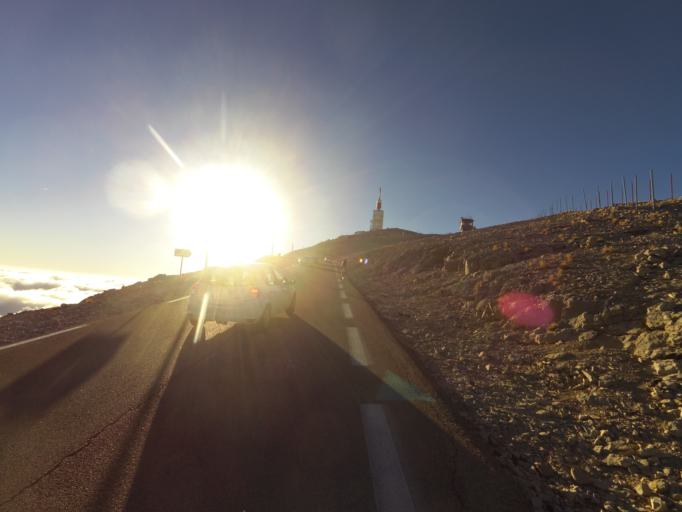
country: FR
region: Rhone-Alpes
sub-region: Departement de la Drome
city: Buis-les-Baronnies
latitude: 44.1742
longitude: 5.2830
